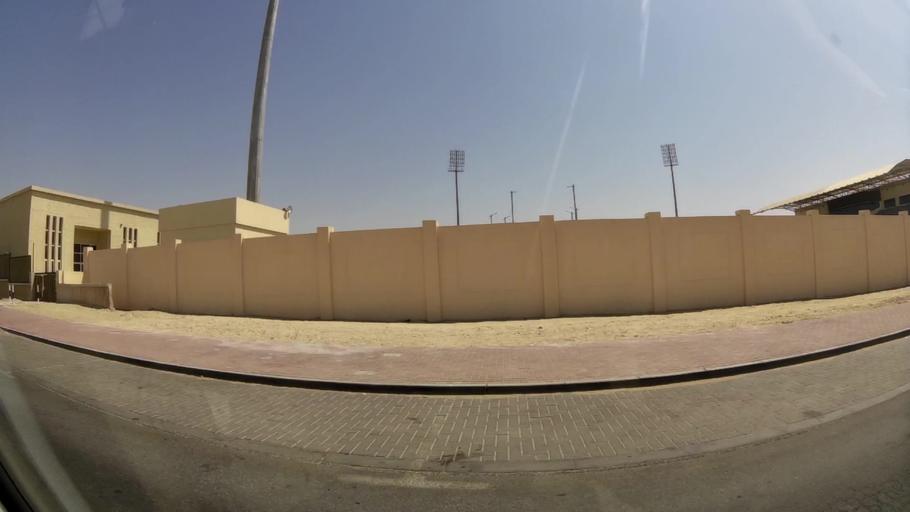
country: AE
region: Ash Shariqah
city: Sharjah
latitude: 25.2790
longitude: 55.3657
